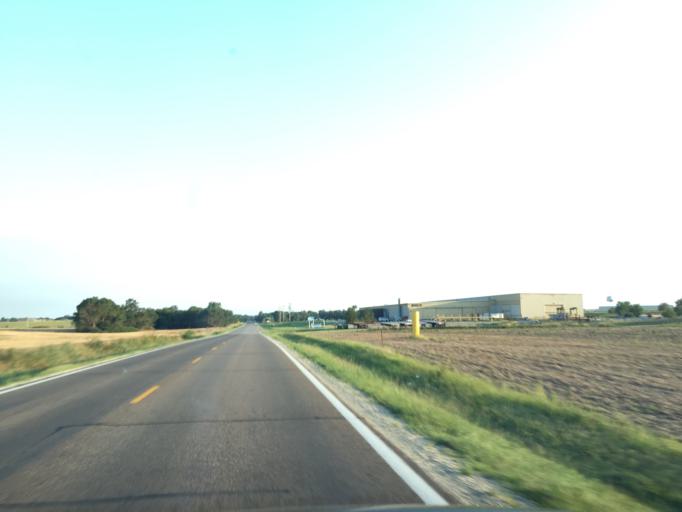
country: US
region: Kansas
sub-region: Ellsworth County
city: Ellsworth
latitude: 38.7515
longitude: -98.2252
